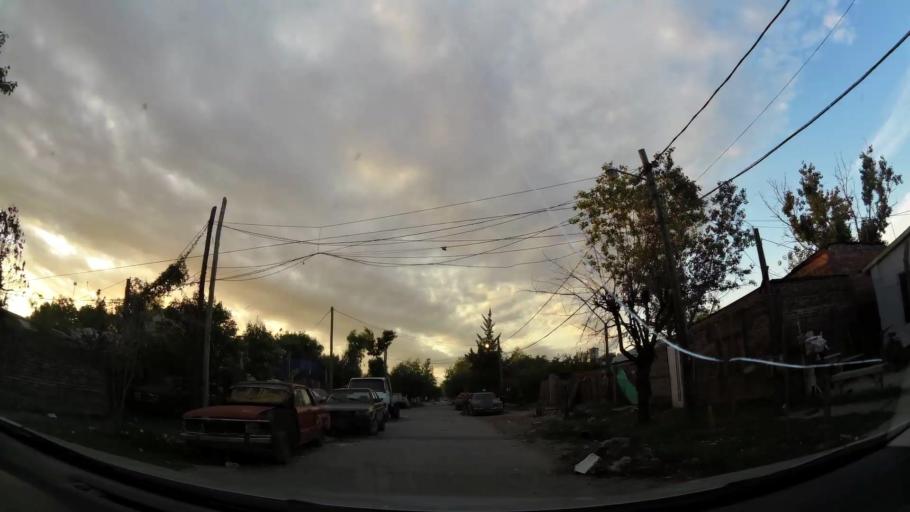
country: AR
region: Buenos Aires
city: Santa Catalina - Dique Lujan
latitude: -34.4394
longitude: -58.6604
